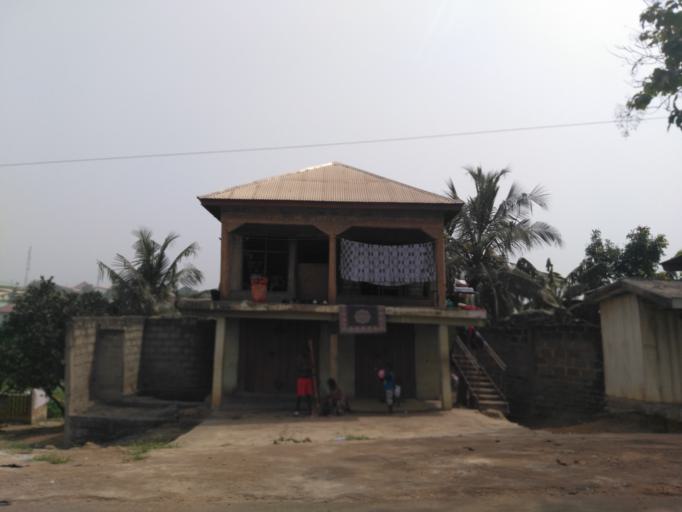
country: GH
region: Ashanti
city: Kumasi
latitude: 6.6449
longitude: -1.6444
